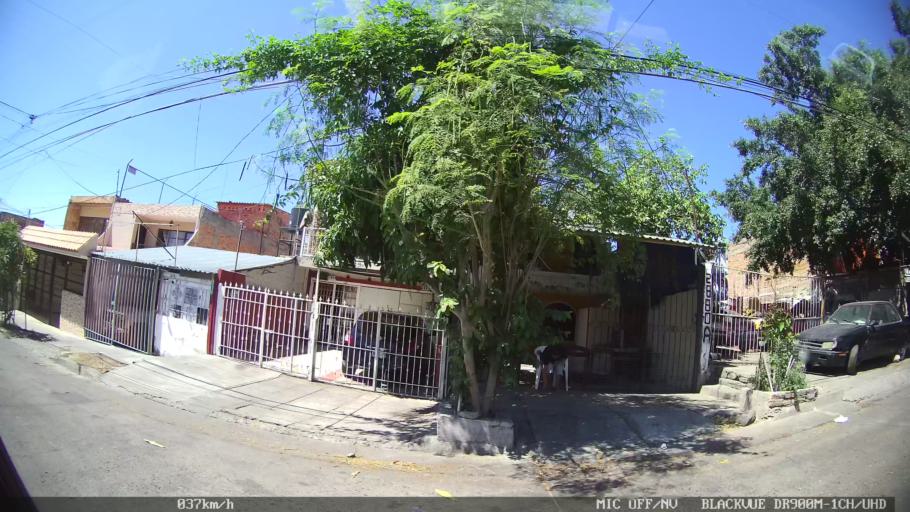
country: MX
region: Jalisco
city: Tlaquepaque
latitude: 20.6968
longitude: -103.2894
